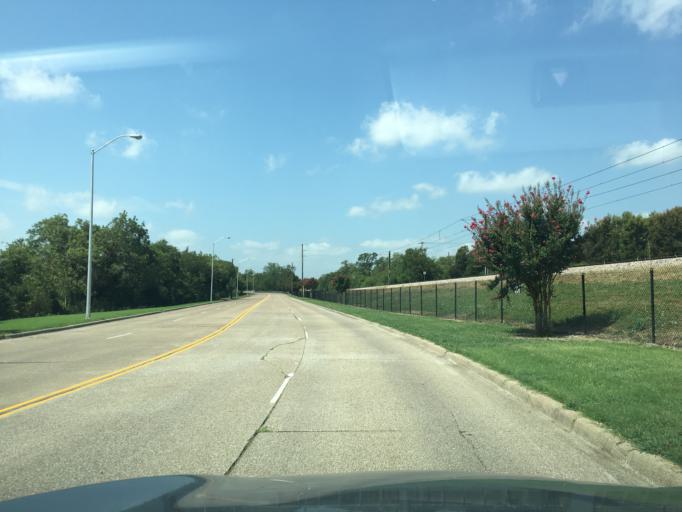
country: US
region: Texas
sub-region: Dallas County
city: Richardson
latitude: 32.9140
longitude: -96.7560
